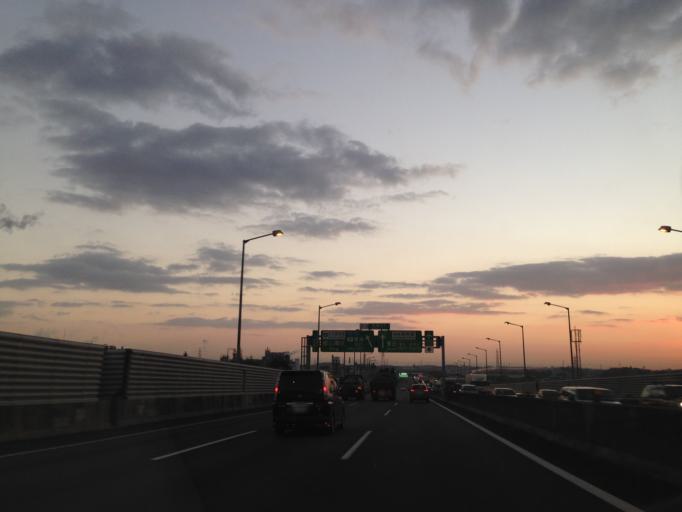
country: JP
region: Aichi
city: Obu
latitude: 35.0521
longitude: 136.8868
